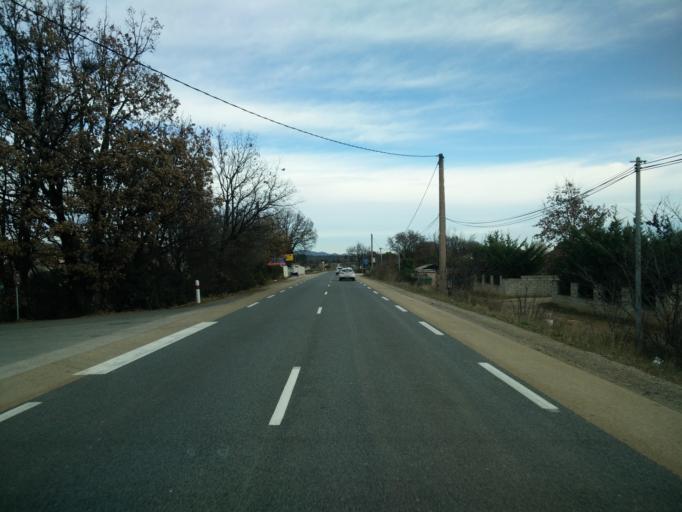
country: FR
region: Provence-Alpes-Cote d'Azur
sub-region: Departement du Var
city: La Motte
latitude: 43.4646
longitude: 6.5367
